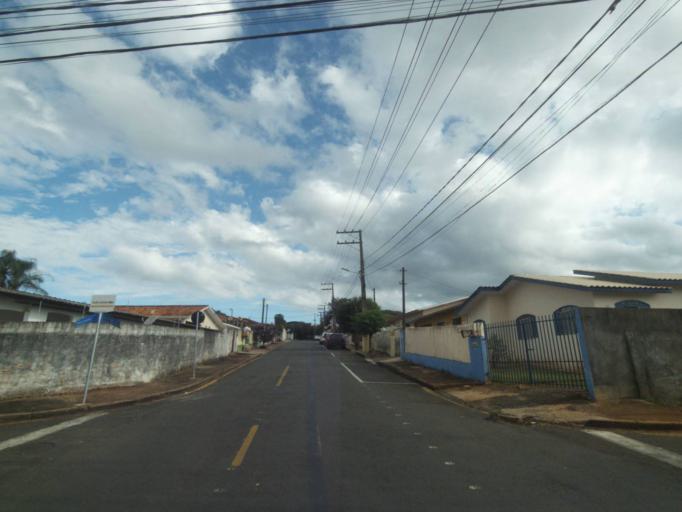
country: BR
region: Parana
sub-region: Telemaco Borba
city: Telemaco Borba
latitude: -24.3375
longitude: -50.6121
